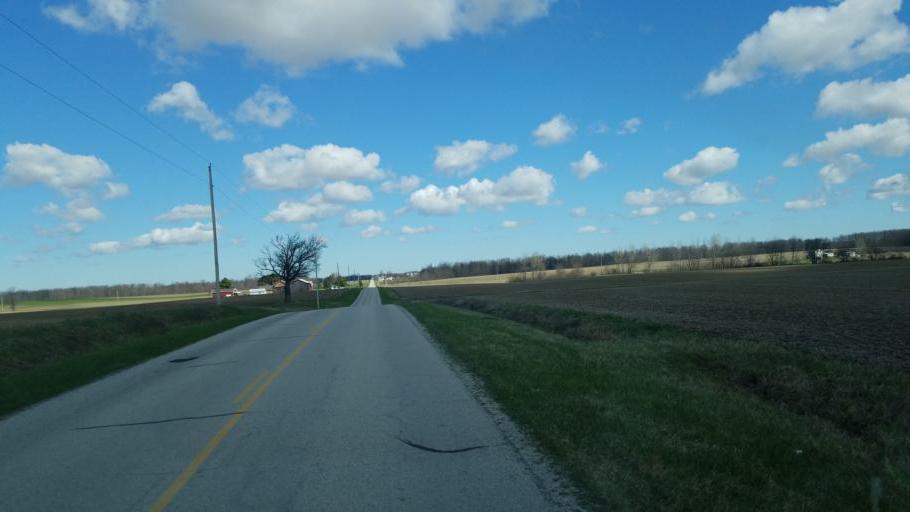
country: US
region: Ohio
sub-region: Sandusky County
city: Mount Carmel
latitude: 41.1422
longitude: -82.9382
